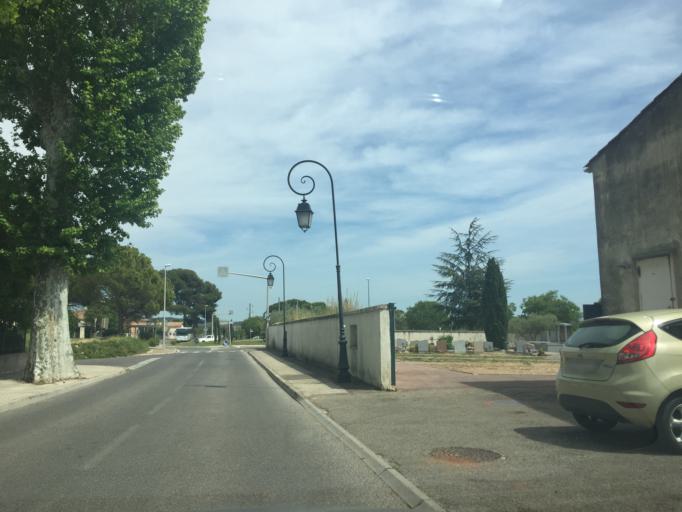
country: FR
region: Provence-Alpes-Cote d'Azur
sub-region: Departement du Var
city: Lorgues
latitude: 43.4922
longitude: 6.3670
